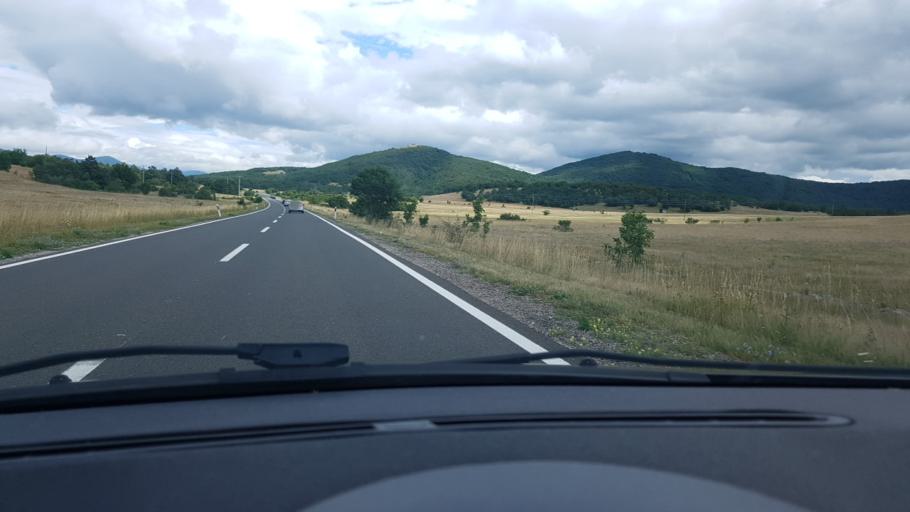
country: HR
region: Zadarska
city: Gracac
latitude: 44.4668
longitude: 15.7997
